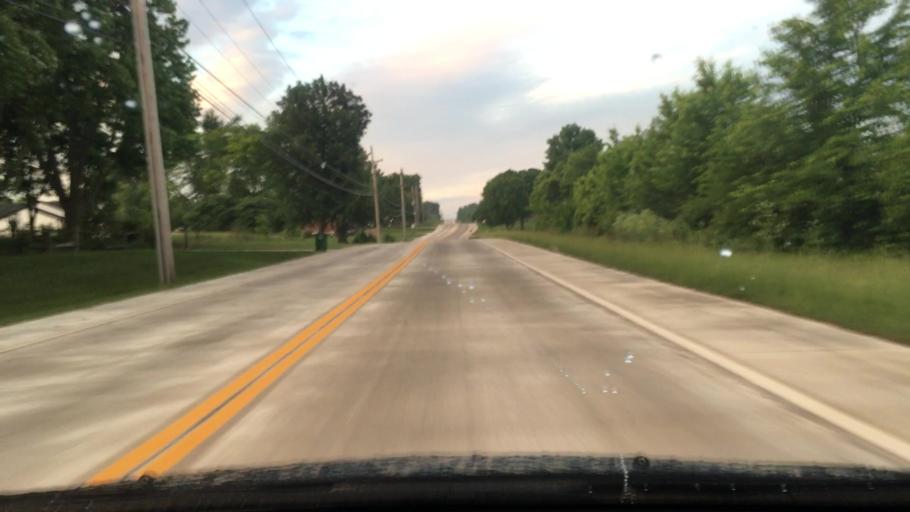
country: US
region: Missouri
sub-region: Jackson County
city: Lees Summit
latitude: 38.8656
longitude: -94.4165
